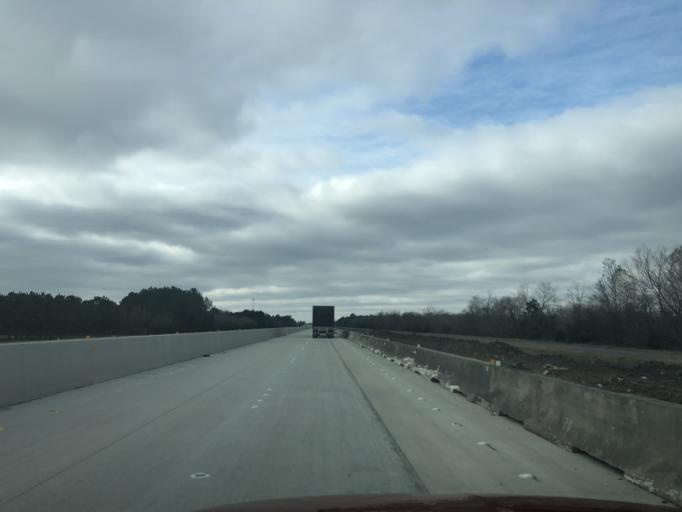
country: US
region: Texas
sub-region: Chambers County
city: Winnie
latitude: 29.8541
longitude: -94.3623
